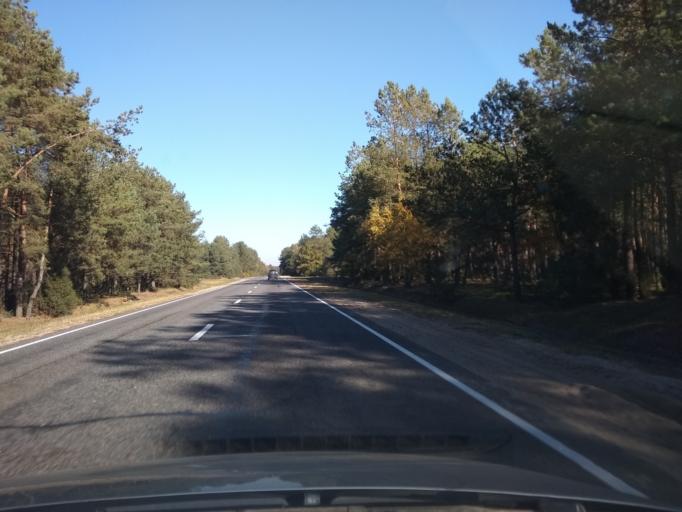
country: BY
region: Brest
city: Kobryn
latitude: 52.1012
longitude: 24.2794
